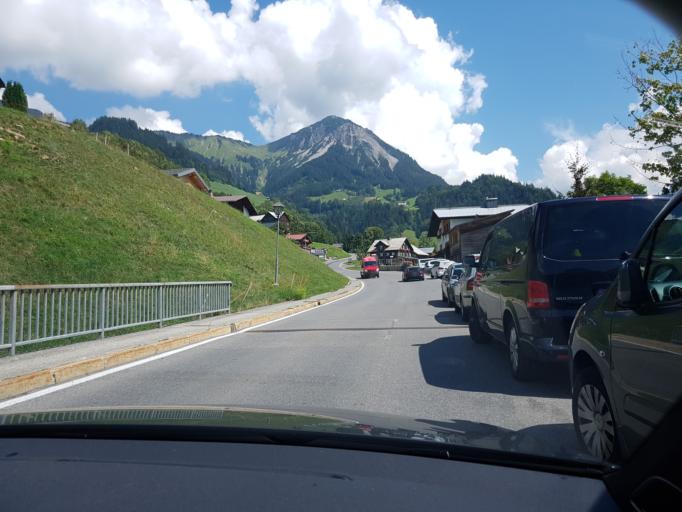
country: AT
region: Vorarlberg
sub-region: Politischer Bezirk Bregenz
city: Damuels
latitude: 47.2414
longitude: 9.9085
